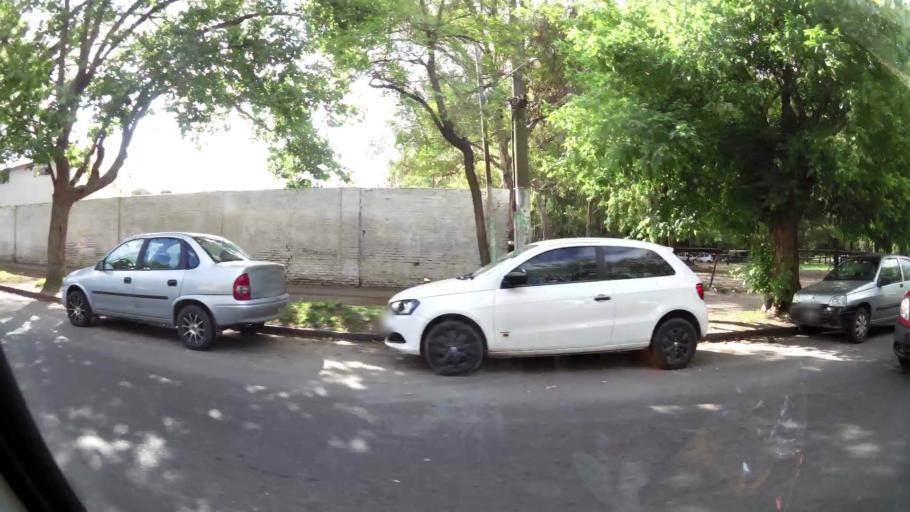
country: AR
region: Buenos Aires
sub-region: Partido de La Plata
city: La Plata
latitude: -34.9141
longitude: -57.9342
